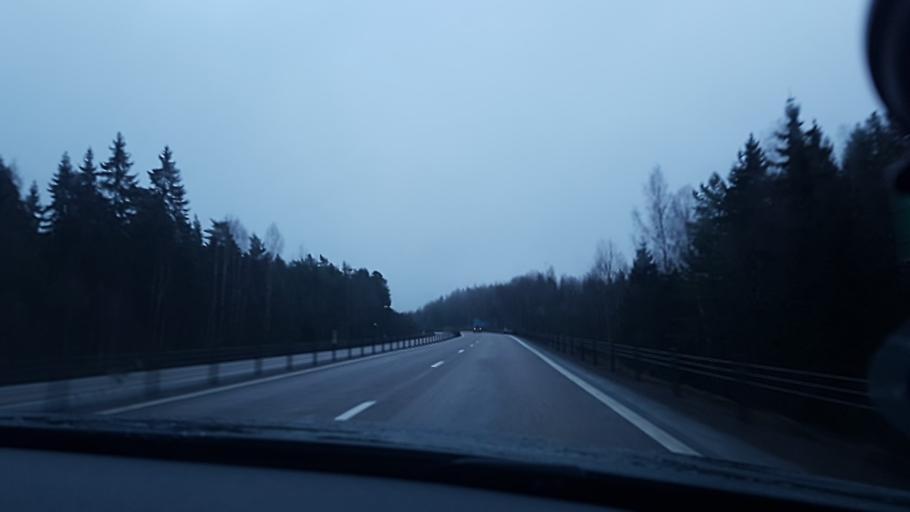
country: SE
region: Vaermland
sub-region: Kristinehamns Kommun
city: Kristinehamn
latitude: 59.3210
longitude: 14.1360
